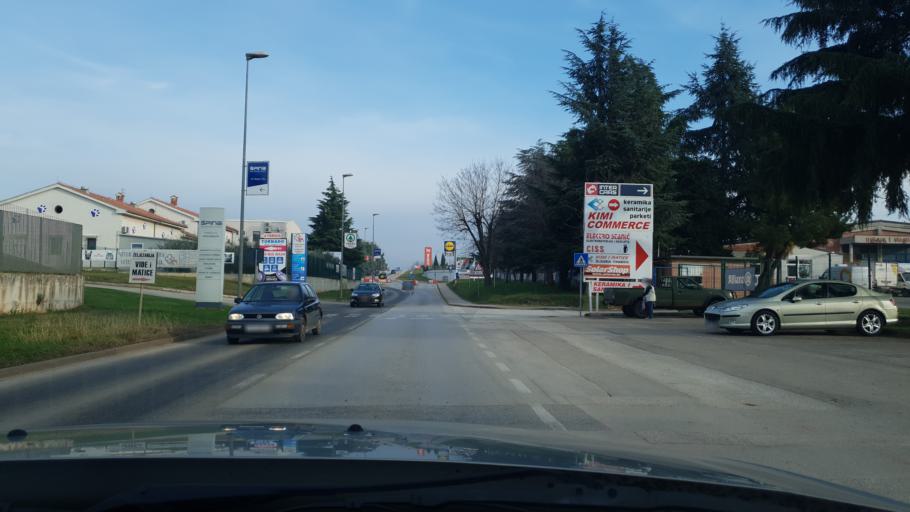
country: HR
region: Istarska
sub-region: Grad Porec
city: Porec
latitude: 45.2305
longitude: 13.6136
